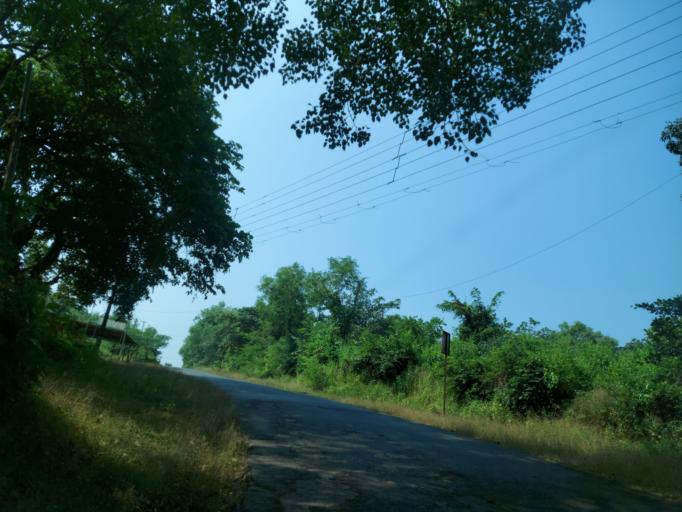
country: IN
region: Maharashtra
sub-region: Sindhudurg
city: Kudal
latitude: 15.9704
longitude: 73.6053
